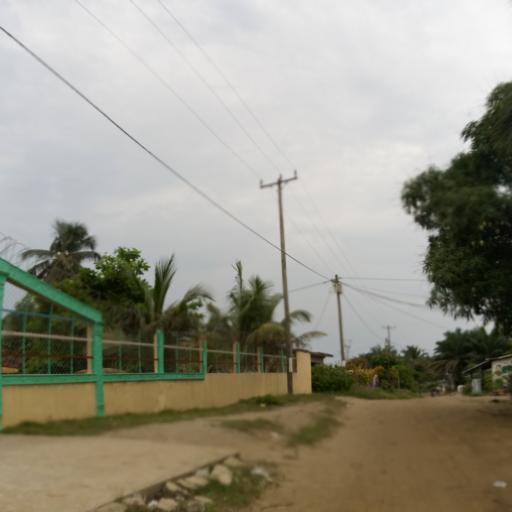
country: LR
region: Montserrado
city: Monrovia
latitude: 6.2908
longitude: -10.6817
